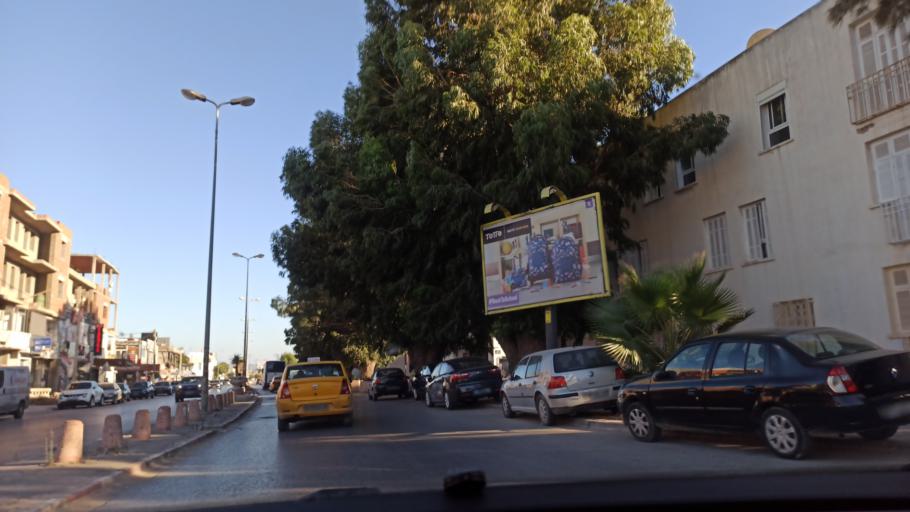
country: TN
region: Tunis
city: La Goulette
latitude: 36.8514
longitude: 10.2582
